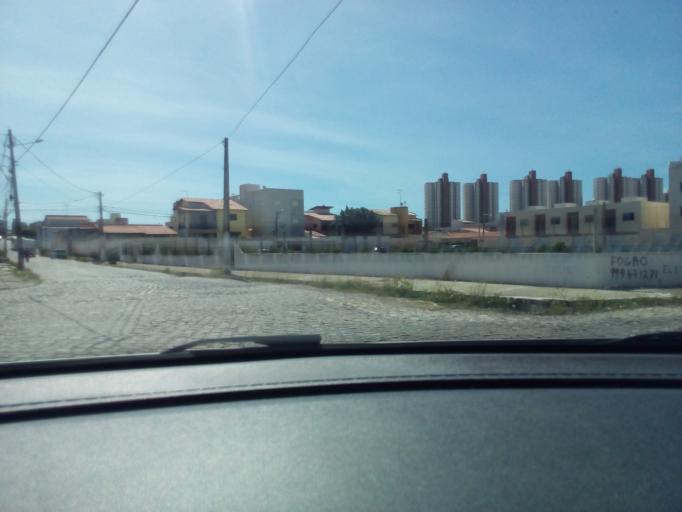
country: BR
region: Rio Grande do Norte
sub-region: Parnamirim
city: Parnamirim
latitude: -5.8893
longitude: -35.1953
